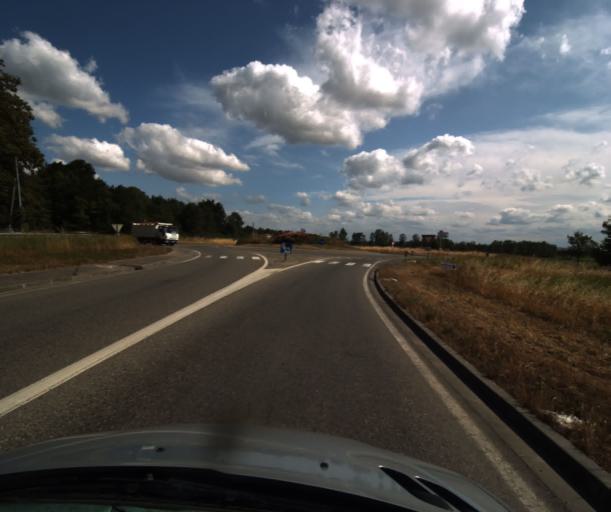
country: FR
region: Midi-Pyrenees
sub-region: Departement du Tarn-et-Garonne
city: Campsas
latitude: 43.8991
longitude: 1.3079
